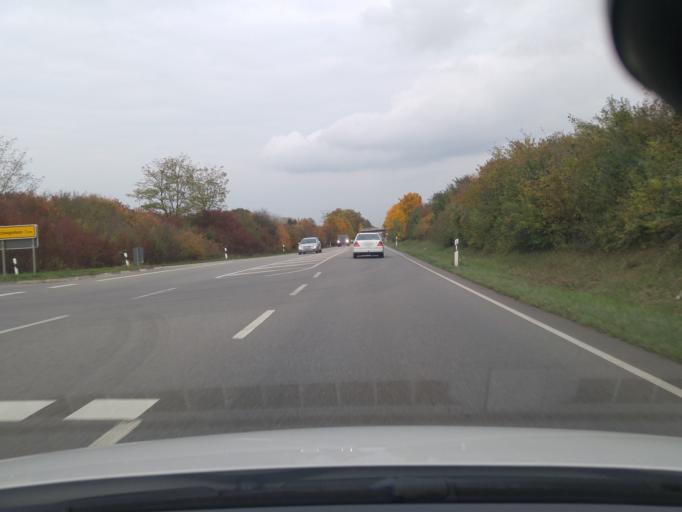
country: DE
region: Rheinland-Pfalz
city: Schwegenheim
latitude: 49.2630
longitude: 8.3182
